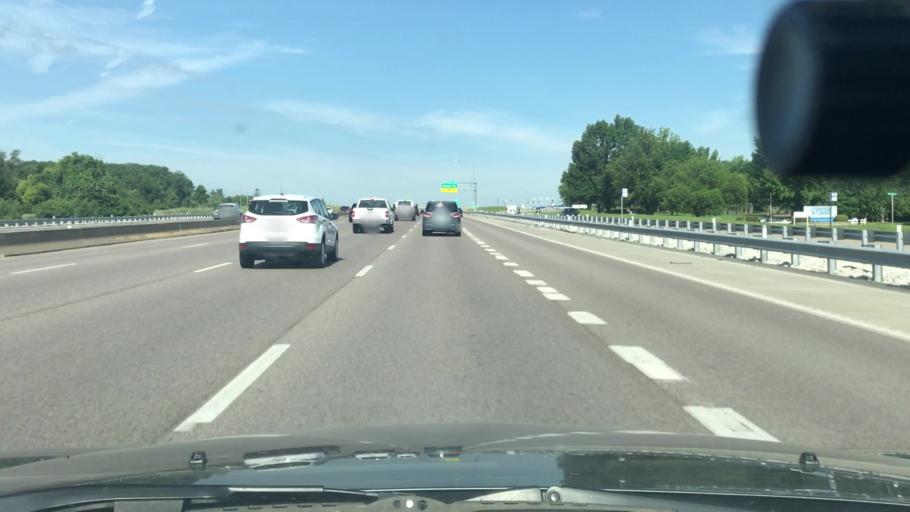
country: US
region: Missouri
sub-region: Saint Louis County
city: Town and Country
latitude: 38.6388
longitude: -90.4744
